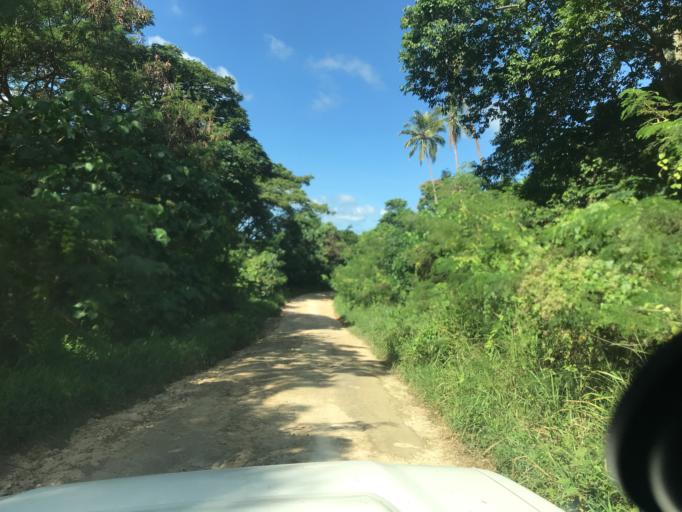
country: VU
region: Sanma
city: Luganville
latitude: -15.5232
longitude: 167.1482
